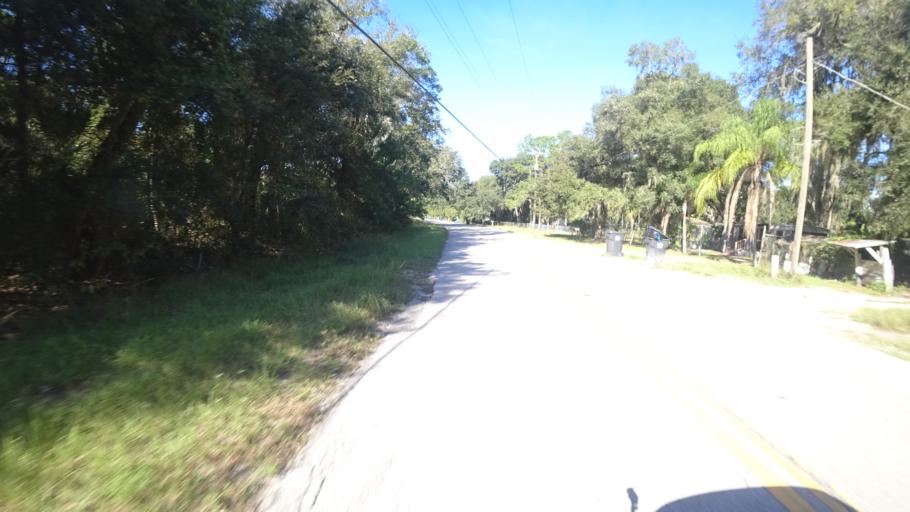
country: US
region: Florida
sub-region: Hillsborough County
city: Sun City Center
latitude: 27.6675
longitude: -82.3379
